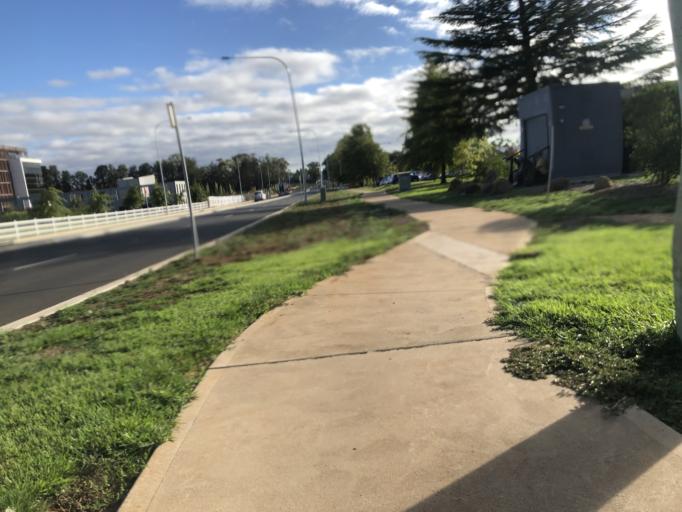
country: AU
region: New South Wales
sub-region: Orange Municipality
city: Orange
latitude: -33.3179
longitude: 149.0900
